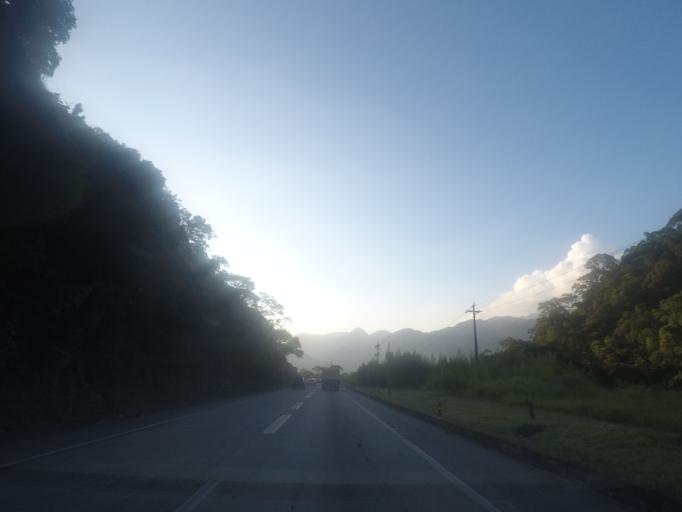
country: BR
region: Rio de Janeiro
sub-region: Petropolis
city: Petropolis
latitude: -22.5218
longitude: -43.2349
